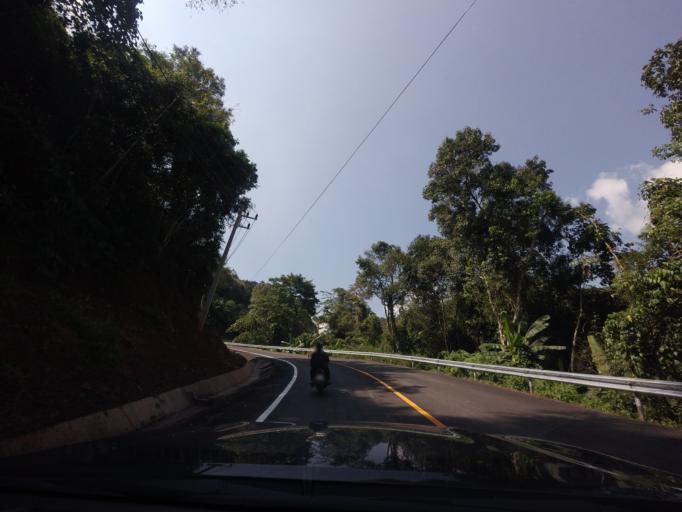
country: TH
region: Nan
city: Bo Kluea
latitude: 19.1866
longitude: 101.1800
